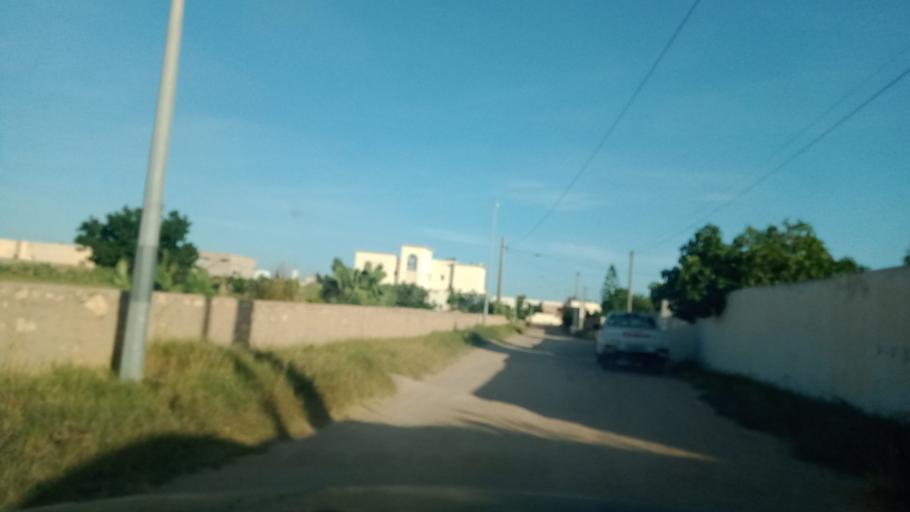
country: TN
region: Safaqis
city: Al Qarmadah
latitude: 34.8153
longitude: 10.7435
